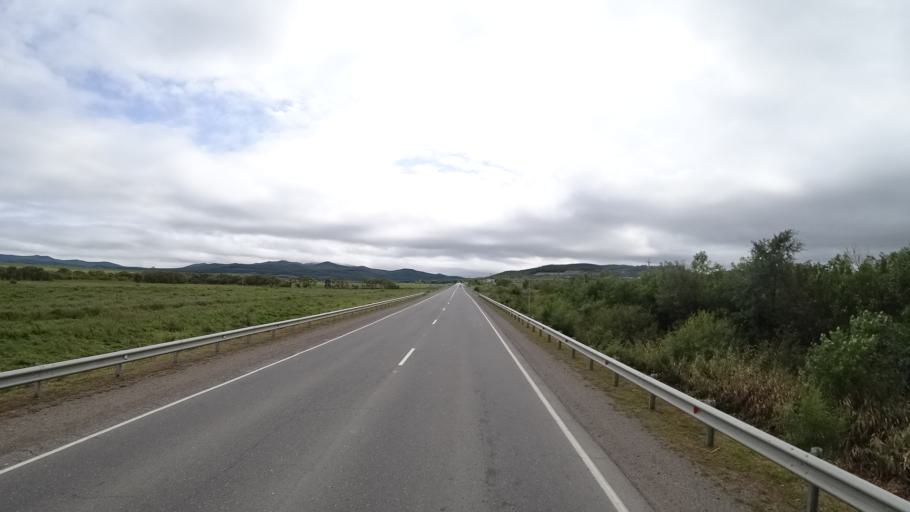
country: RU
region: Primorskiy
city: Monastyrishche
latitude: 44.1781
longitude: 132.4413
